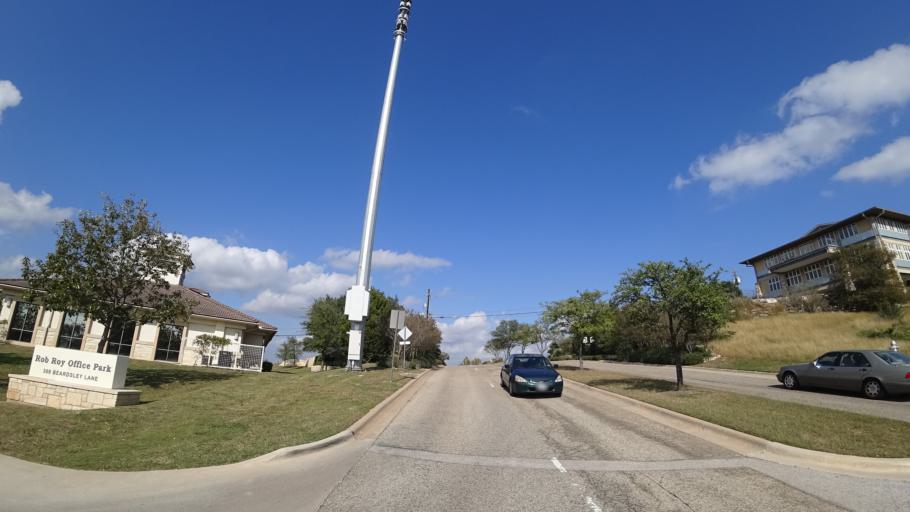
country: US
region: Texas
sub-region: Travis County
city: Lost Creek
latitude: 30.3126
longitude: -97.8532
